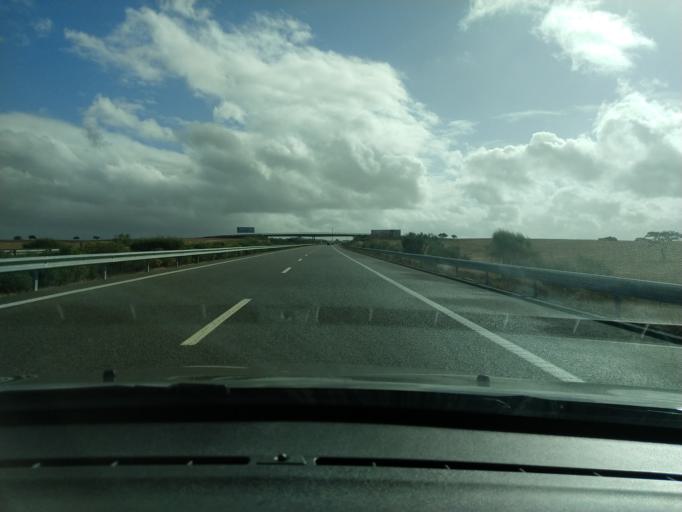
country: PT
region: Beja
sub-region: Ourique
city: Ourique
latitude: 37.6351
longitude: -8.1569
